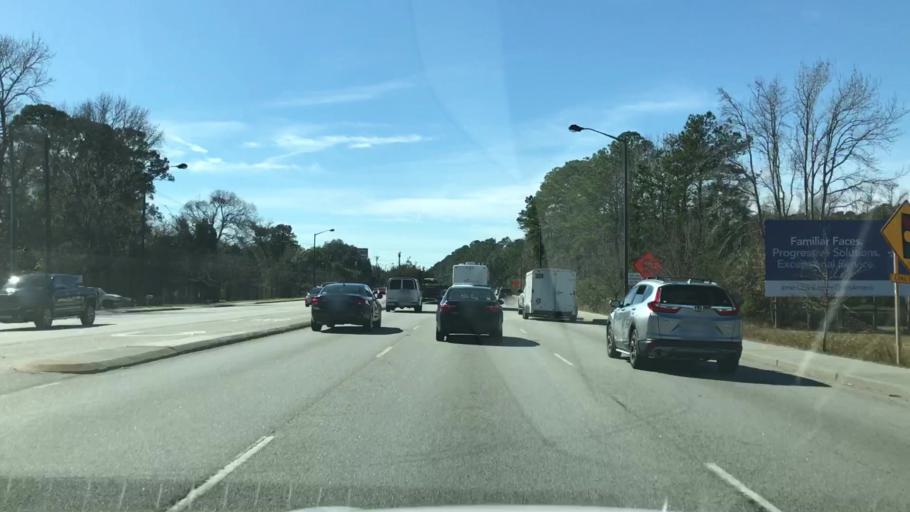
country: US
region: South Carolina
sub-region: Charleston County
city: Isle of Palms
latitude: 32.8465
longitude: -79.8119
